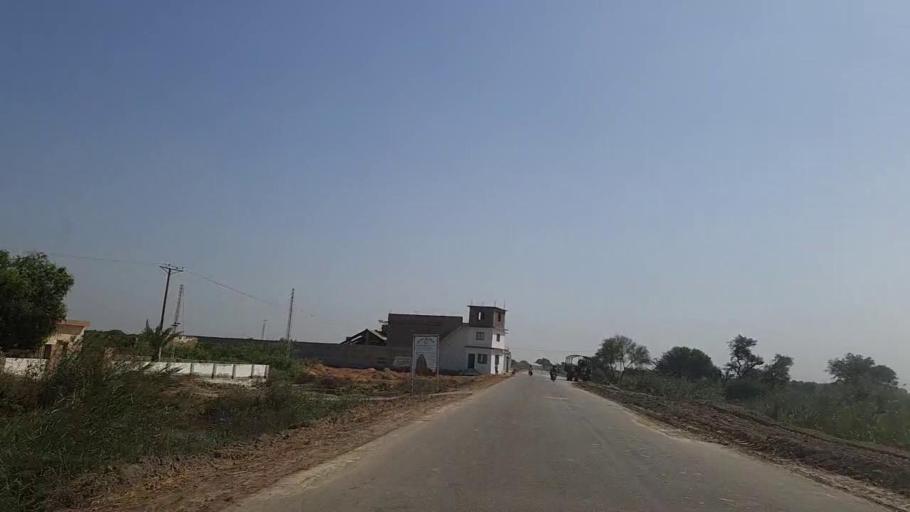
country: PK
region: Sindh
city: Daro Mehar
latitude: 24.7787
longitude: 68.2009
